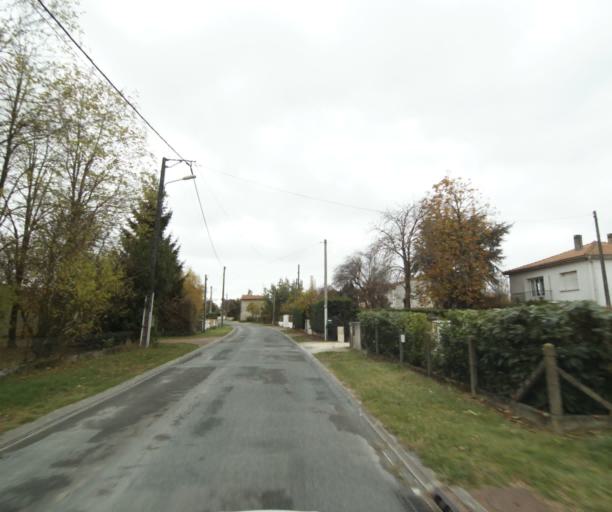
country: FR
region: Poitou-Charentes
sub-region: Departement de la Charente-Maritime
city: Fontcouverte
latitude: 45.7578
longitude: -0.5836
